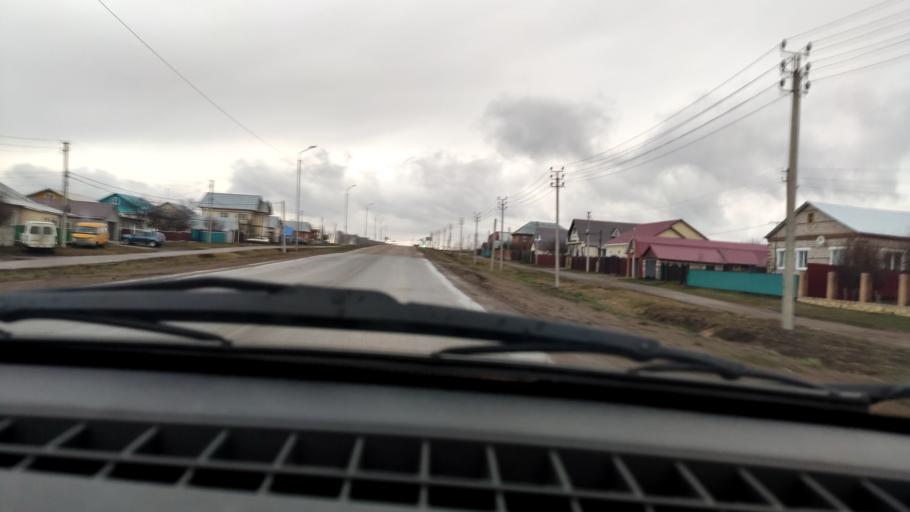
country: RU
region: Bashkortostan
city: Chekmagush
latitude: 55.1391
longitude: 54.6355
